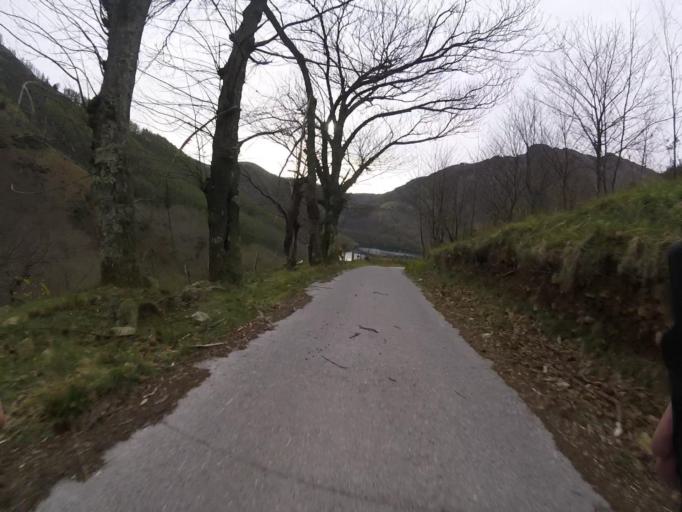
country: ES
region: Navarre
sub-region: Provincia de Navarra
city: Lesaka
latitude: 43.2743
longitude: -1.7646
